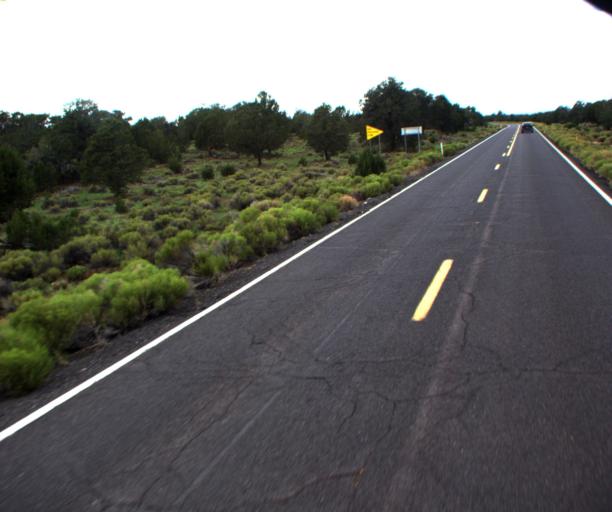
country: US
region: Arizona
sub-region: Coconino County
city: Parks
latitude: 35.5392
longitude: -111.8531
